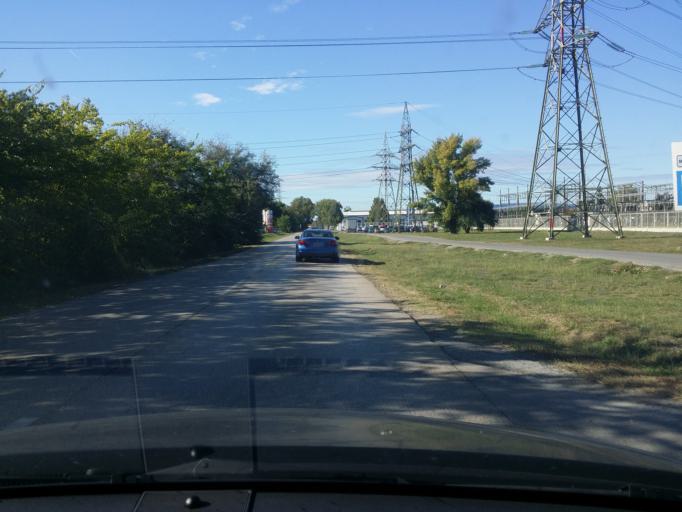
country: HU
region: Pest
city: God
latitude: 47.6906
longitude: 19.1613
